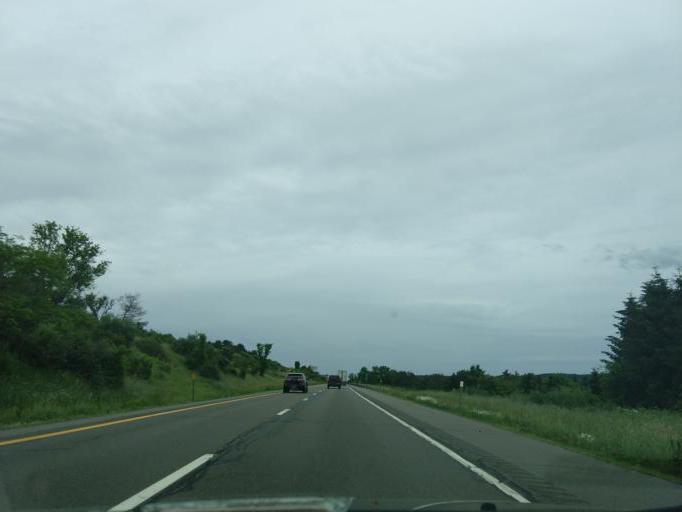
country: US
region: New York
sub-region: Chenango County
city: Lakeview
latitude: 42.4230
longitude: -76.0184
